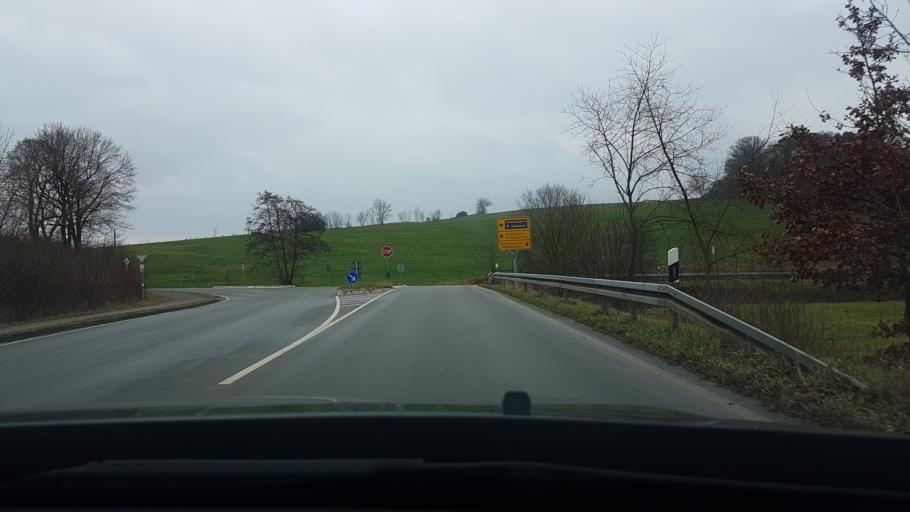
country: DE
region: Hesse
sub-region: Regierungsbezirk Kassel
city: Volkmarsen
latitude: 51.3931
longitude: 9.0743
